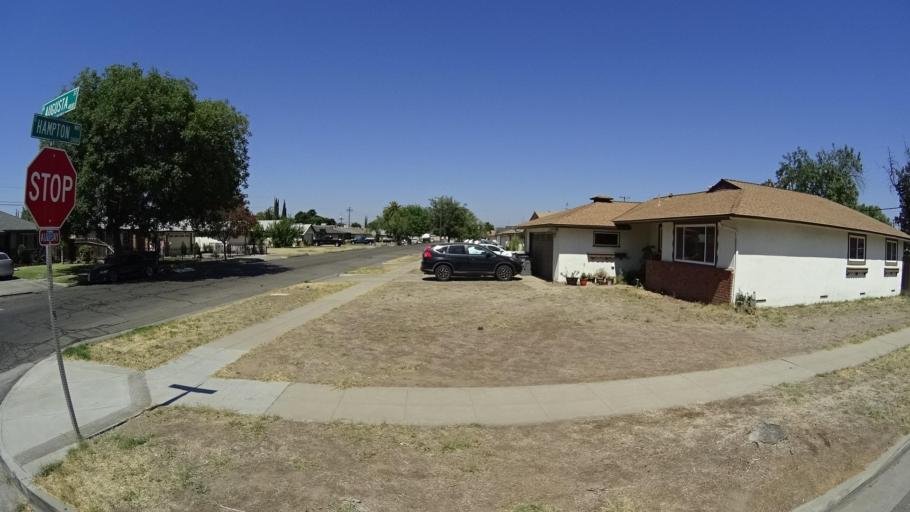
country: US
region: California
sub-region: Fresno County
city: Fresno
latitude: 36.7920
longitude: -119.7792
